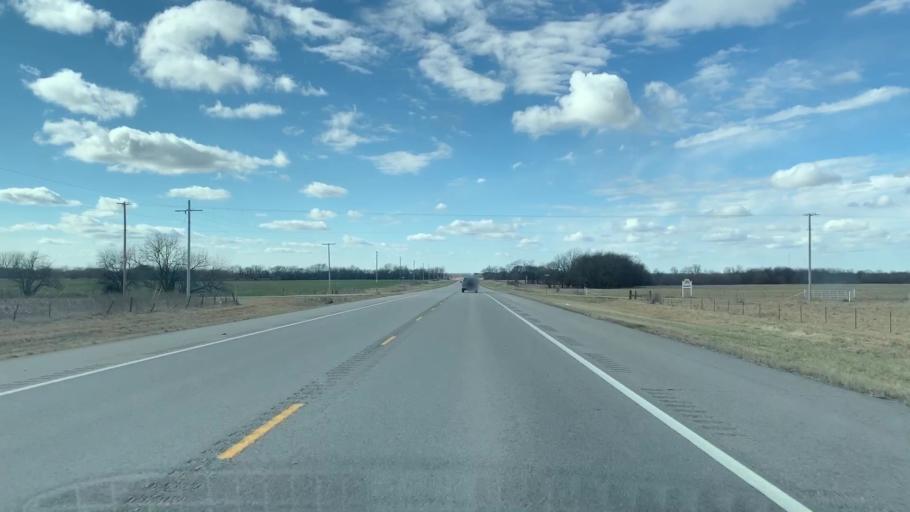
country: US
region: Kansas
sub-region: Labette County
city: Oswego
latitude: 37.3401
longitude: -95.0303
